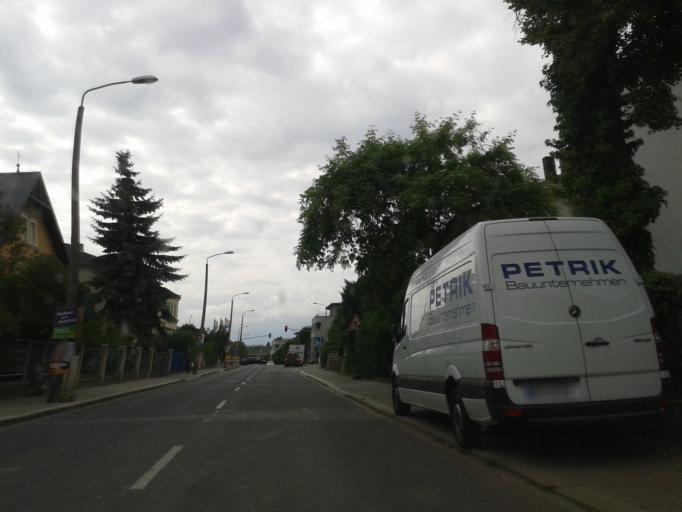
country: DE
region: Saxony
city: Dresden
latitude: 51.0317
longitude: 13.7124
